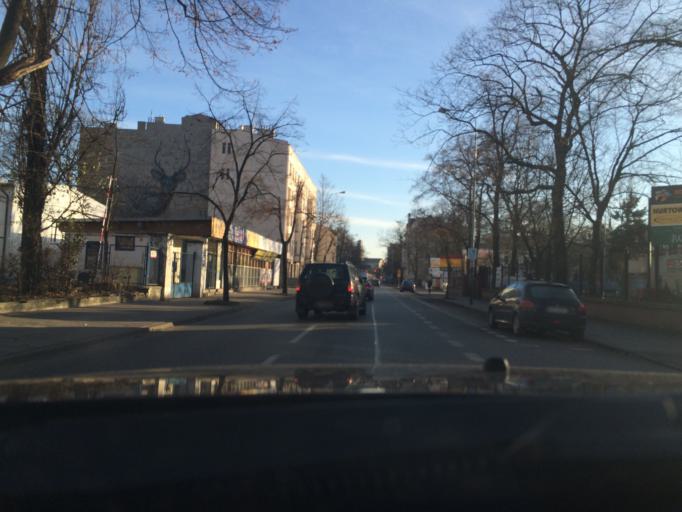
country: PL
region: Lodz Voivodeship
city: Lodz
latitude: 51.7632
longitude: 19.4395
